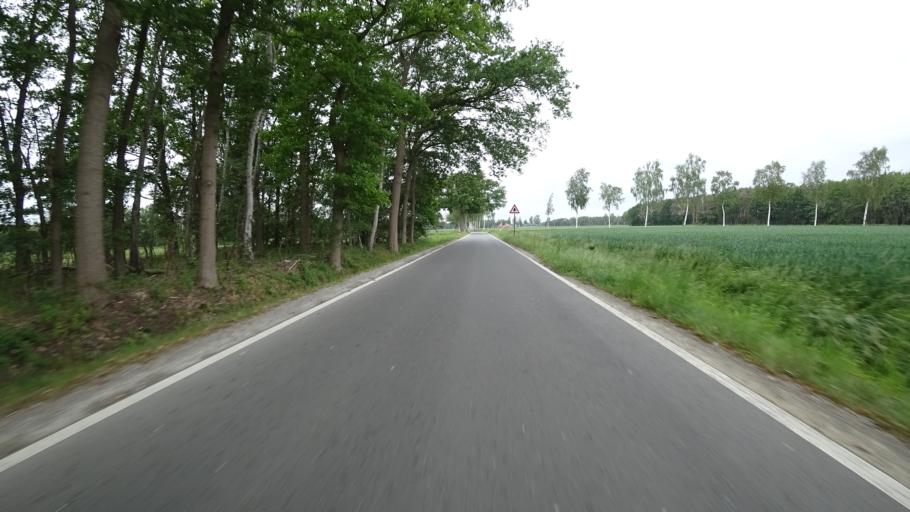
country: DE
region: North Rhine-Westphalia
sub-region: Regierungsbezirk Detmold
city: Rheda-Wiedenbruck
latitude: 51.8412
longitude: 8.3579
